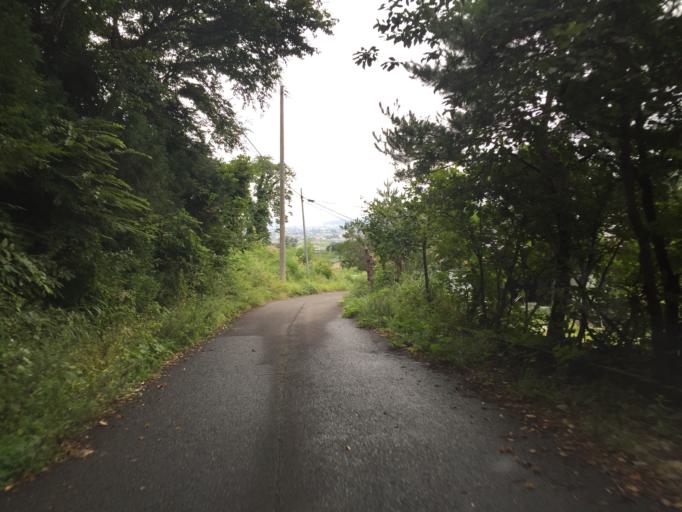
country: JP
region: Fukushima
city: Fukushima-shi
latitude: 37.7967
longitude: 140.3793
